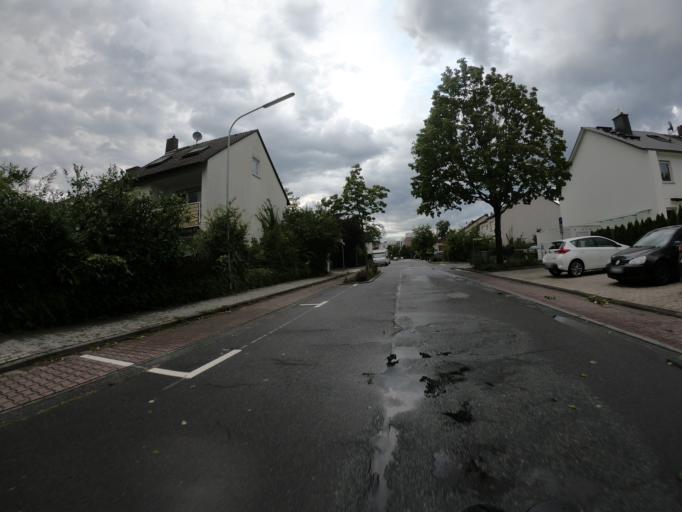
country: DE
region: Hesse
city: Langen
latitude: 50.0042
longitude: 8.6465
